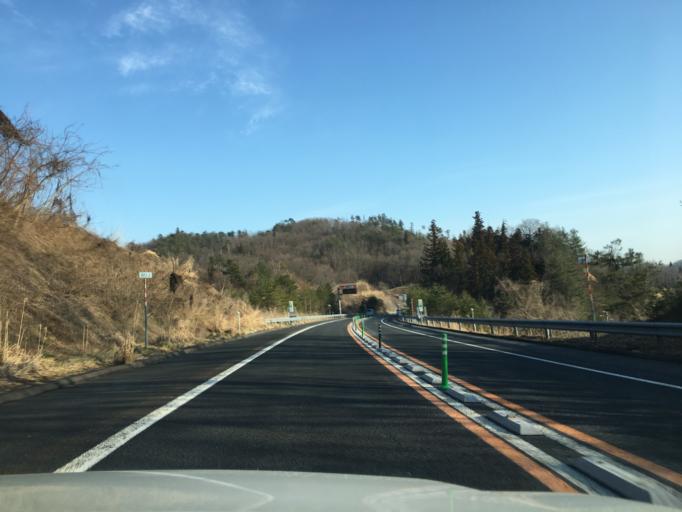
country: JP
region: Yamagata
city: Sagae
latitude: 38.3890
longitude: 140.2192
